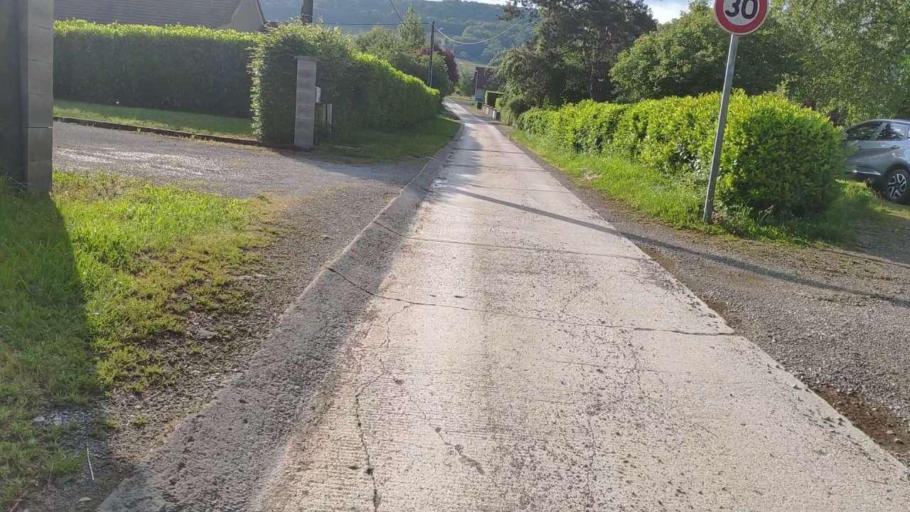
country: FR
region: Franche-Comte
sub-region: Departement du Jura
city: Perrigny
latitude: 46.7291
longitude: 5.5916
